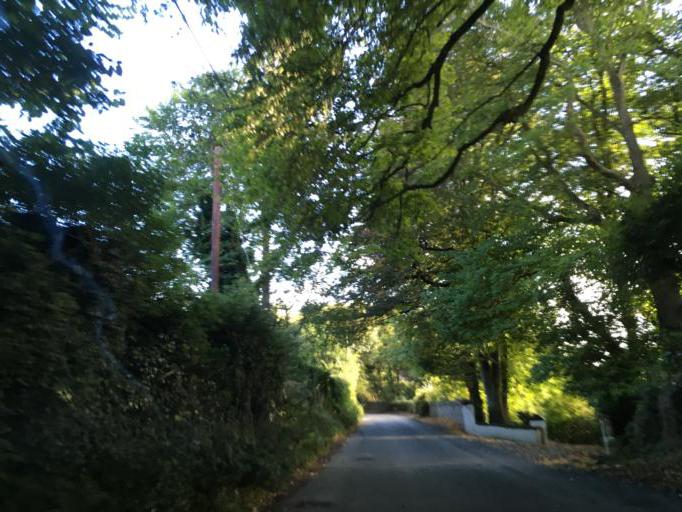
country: IE
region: Leinster
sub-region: Wicklow
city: Wicklow
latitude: 52.9160
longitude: -6.0808
